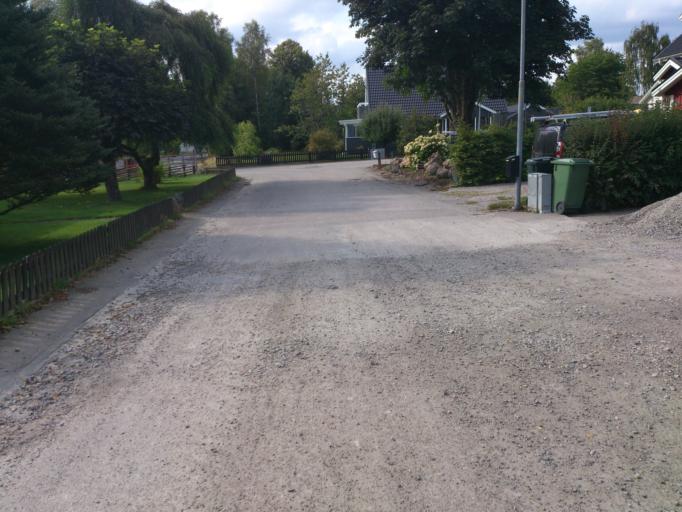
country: SE
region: Kronoberg
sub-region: Alvesta Kommun
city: Moheda
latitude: 56.9935
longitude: 14.5846
